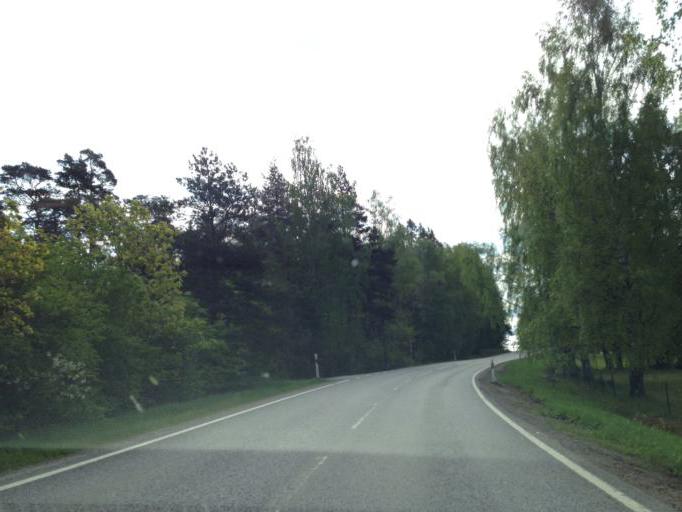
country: SE
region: Soedermanland
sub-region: Nykopings Kommun
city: Svalsta
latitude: 58.8659
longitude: 16.9051
